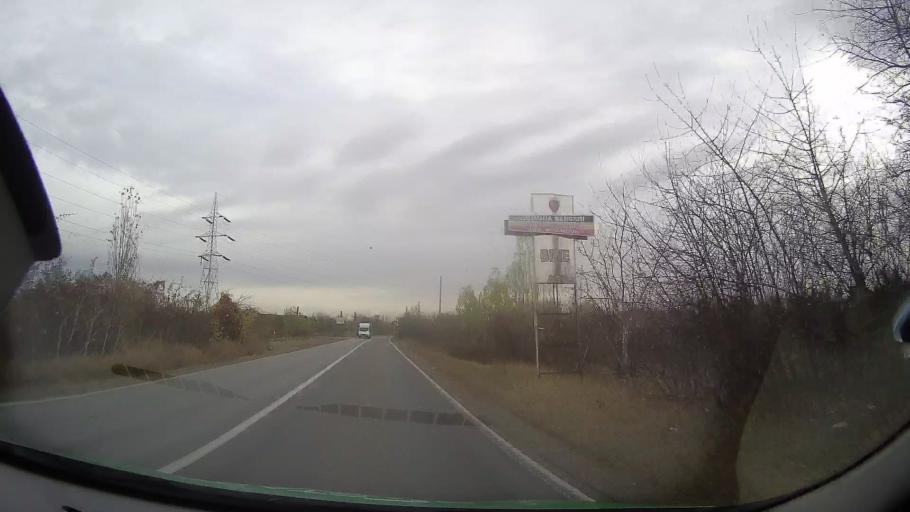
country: RO
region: Prahova
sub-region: Comuna Bucov
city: Bucov
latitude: 44.9495
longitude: 26.0965
